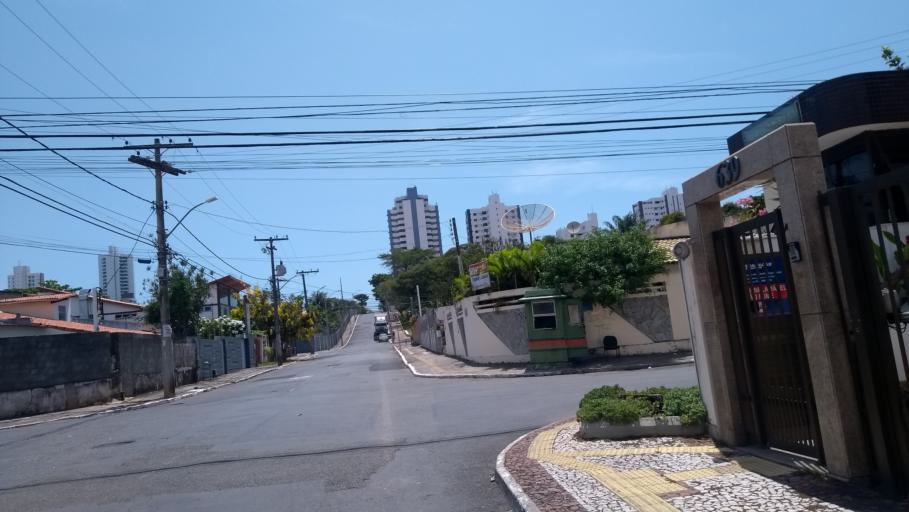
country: BR
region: Bahia
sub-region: Salvador
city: Salvador
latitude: -12.9915
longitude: -38.4601
